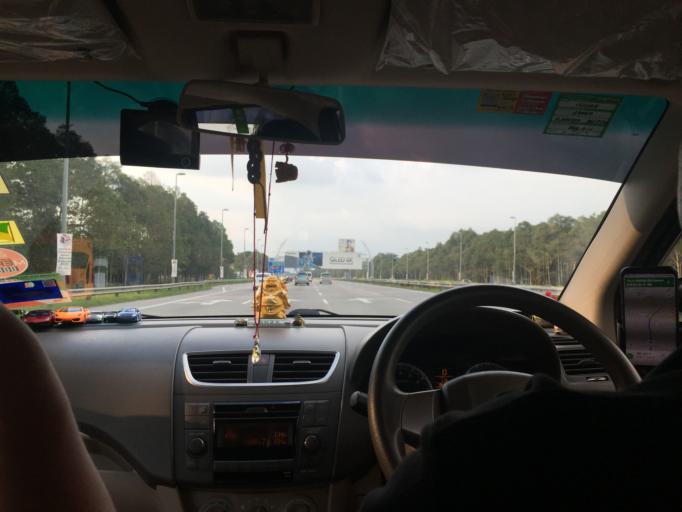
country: MY
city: Sungai Pelek New Village
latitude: 2.7666
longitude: 101.6833
